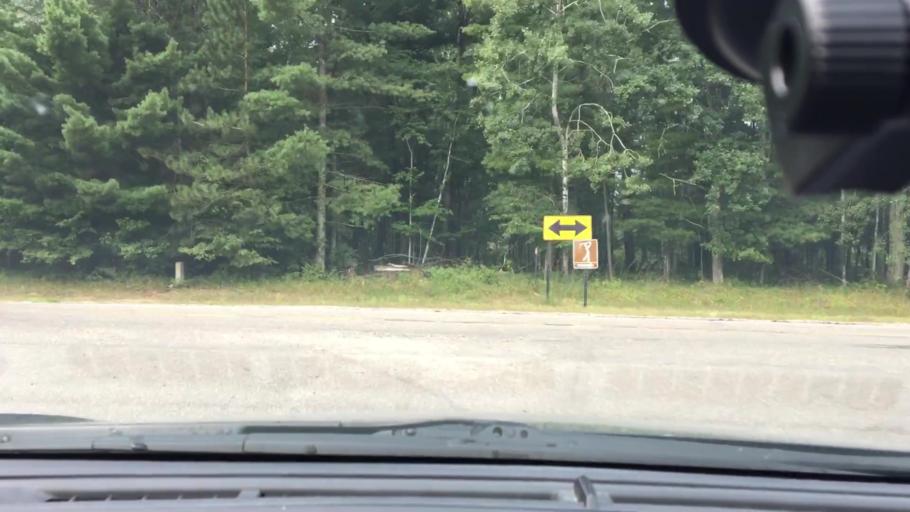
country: US
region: Minnesota
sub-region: Crow Wing County
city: Cross Lake
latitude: 46.6603
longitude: -94.0982
